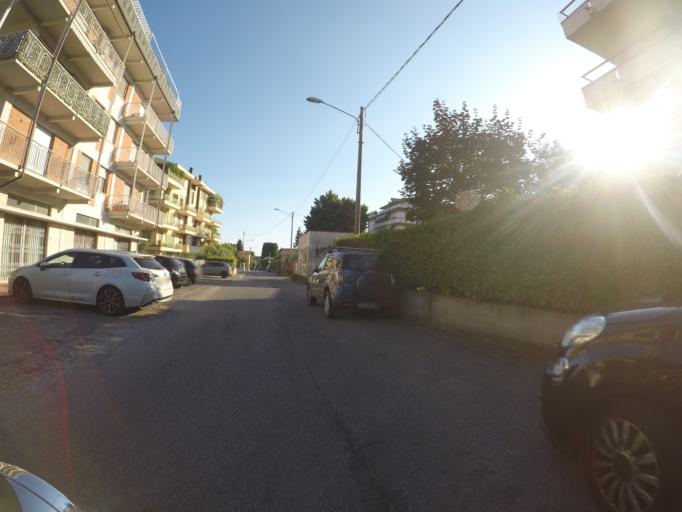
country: IT
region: Tuscany
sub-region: Provincia di Massa-Carrara
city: Massa
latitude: 44.0313
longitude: 10.1368
